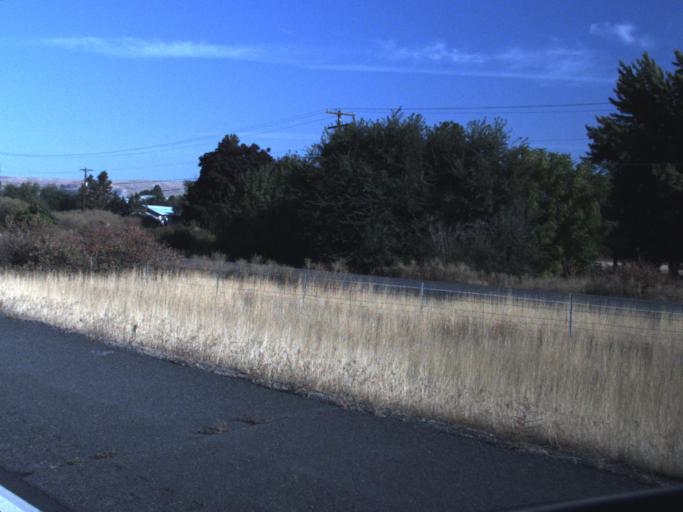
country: US
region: Washington
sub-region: Yakima County
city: Gleed
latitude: 46.6530
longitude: -120.6112
